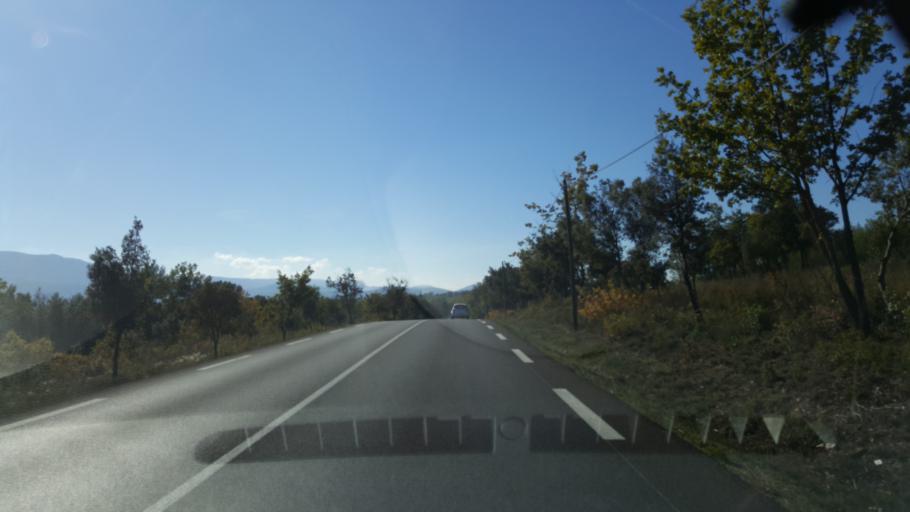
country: FR
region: Provence-Alpes-Cote d'Azur
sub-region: Departement du Var
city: Rougiers
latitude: 43.4187
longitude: 5.8330
